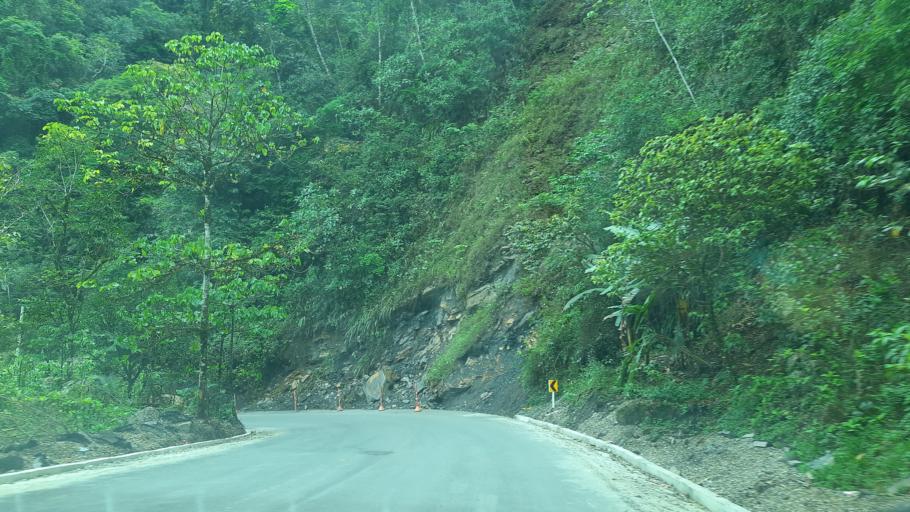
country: CO
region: Boyaca
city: Santa Maria
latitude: 4.8648
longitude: -73.2334
